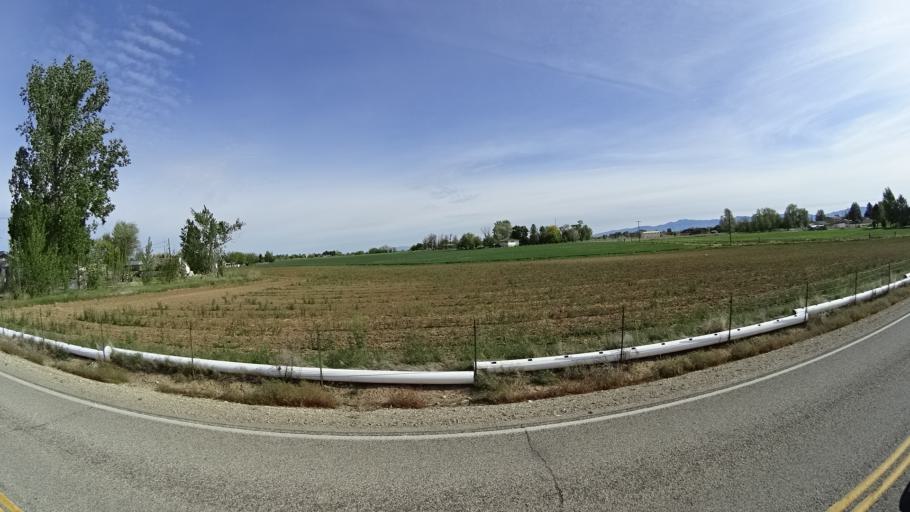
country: US
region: Idaho
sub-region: Ada County
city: Kuna
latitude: 43.4736
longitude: -116.3657
